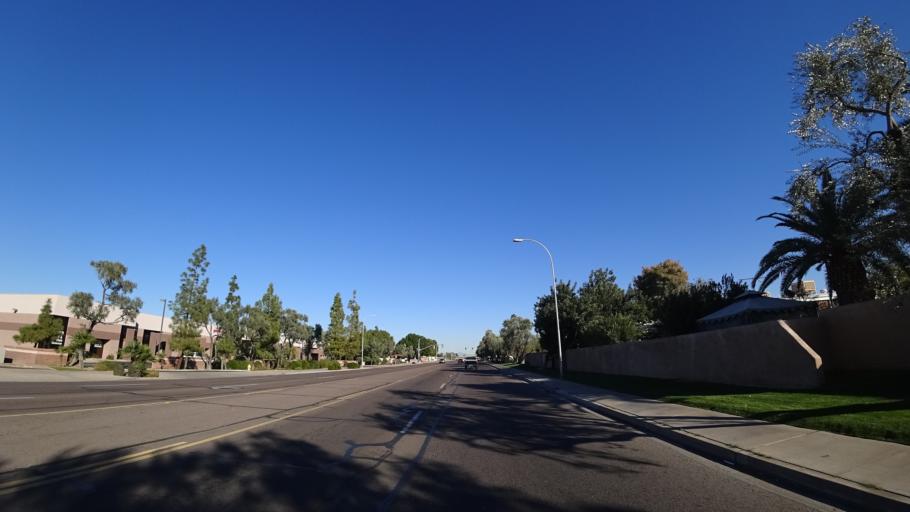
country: US
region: Arizona
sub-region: Maricopa County
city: Guadalupe
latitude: 33.3927
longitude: -111.9741
